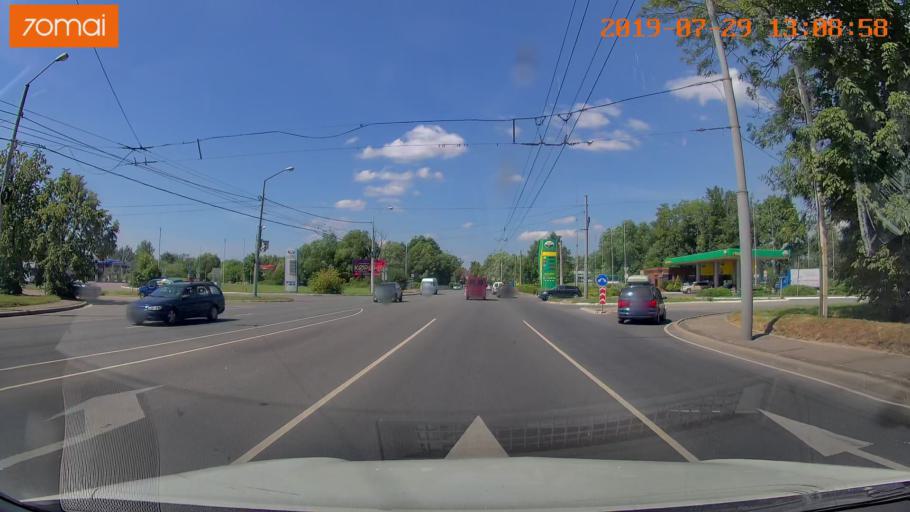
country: RU
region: Kaliningrad
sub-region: Gorod Kaliningrad
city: Kaliningrad
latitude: 54.7127
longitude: 20.4233
